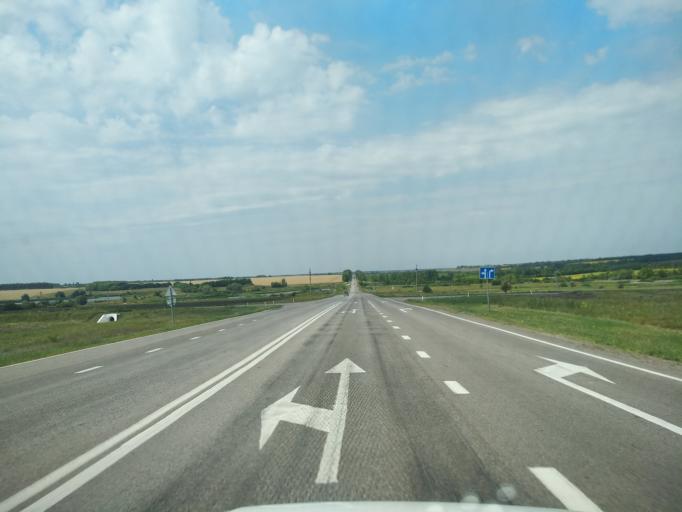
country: RU
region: Voronezj
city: Verkhnyaya Khava
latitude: 51.7035
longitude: 39.9769
